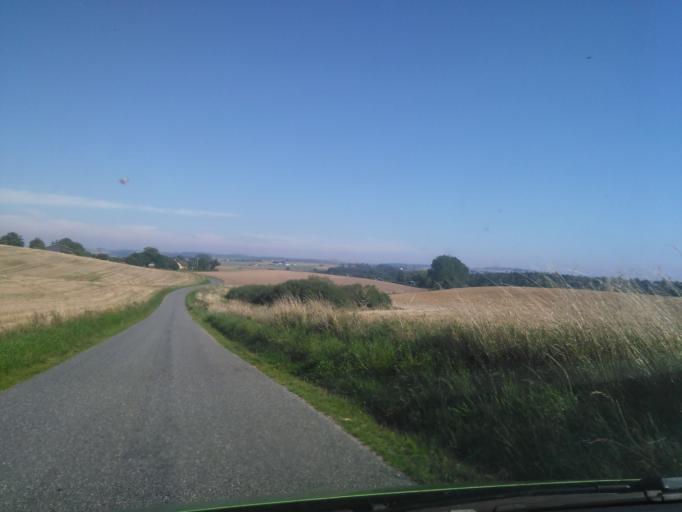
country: DK
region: Central Jutland
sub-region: Syddjurs Kommune
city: Ronde
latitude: 56.1836
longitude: 10.4347
